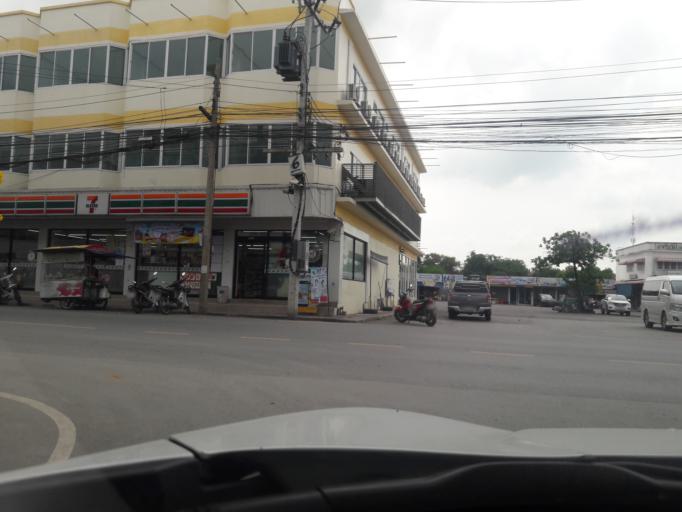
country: TH
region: Lop Buri
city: Ban Mi
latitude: 15.0427
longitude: 100.5430
